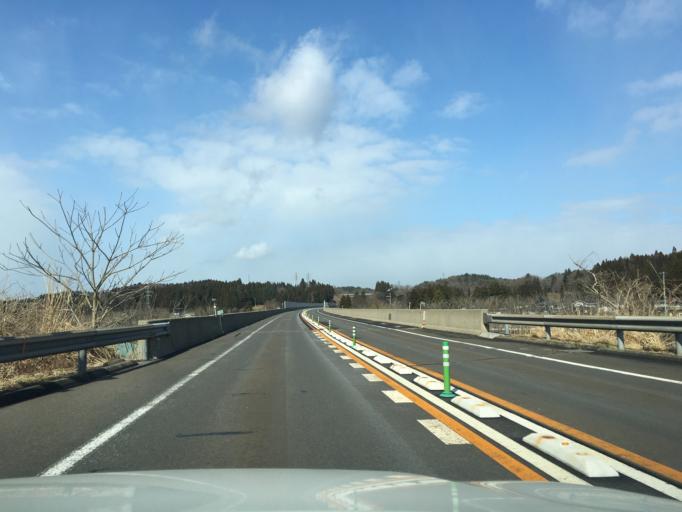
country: JP
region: Akita
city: Akita
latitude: 39.7538
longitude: 140.1414
